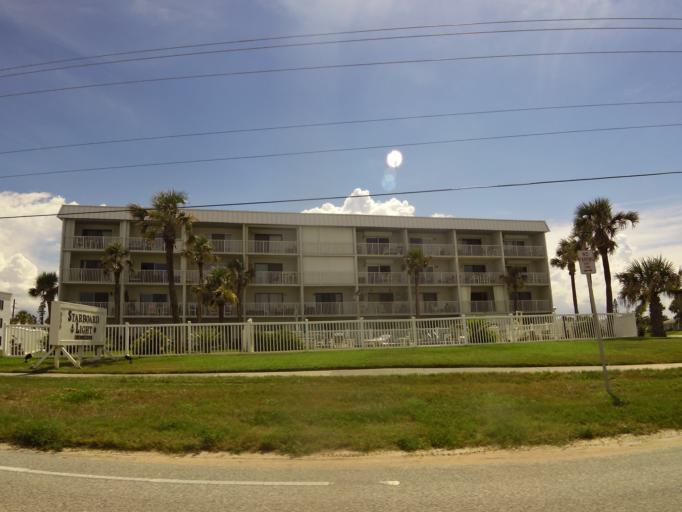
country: US
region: Florida
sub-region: Volusia County
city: Ormond-by-the-Sea
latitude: 29.3428
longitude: -81.0634
